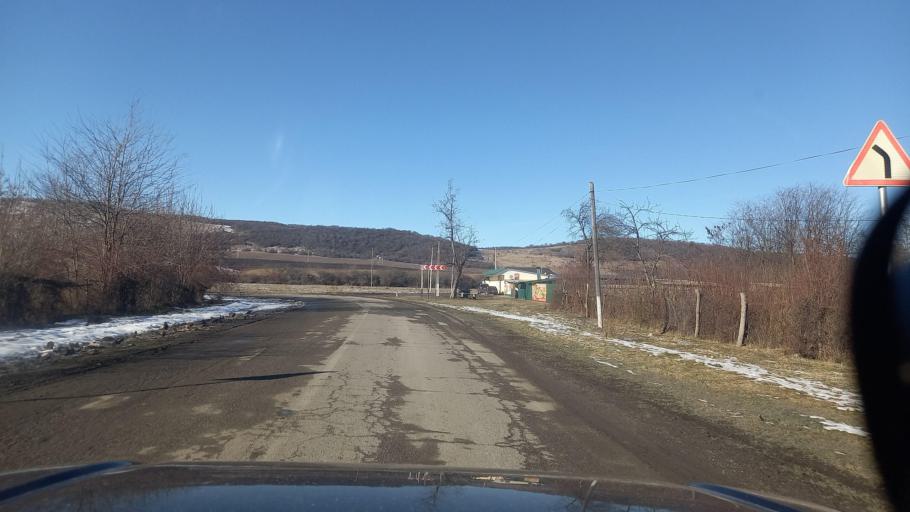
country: RU
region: Kabardino-Balkariya
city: Urukh
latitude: 43.2664
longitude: 43.9888
